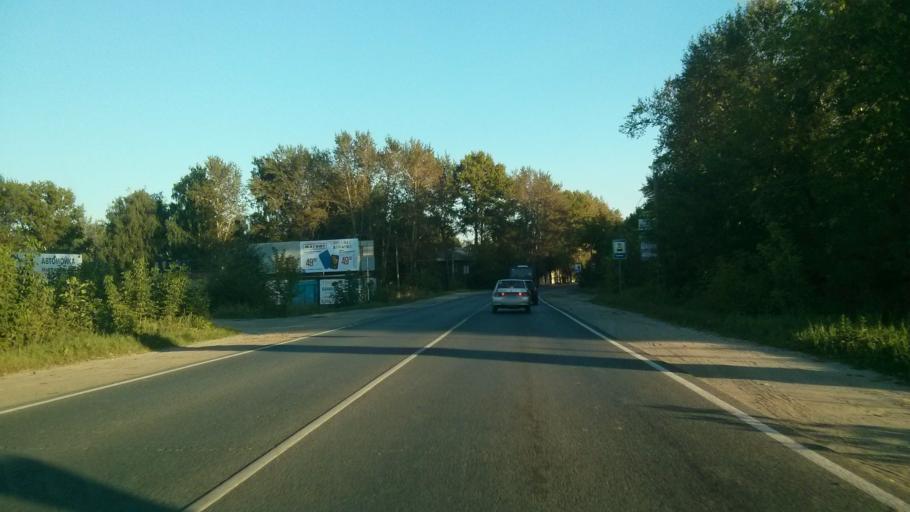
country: RU
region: Vladimir
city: Murom
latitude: 55.5983
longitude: 42.0327
